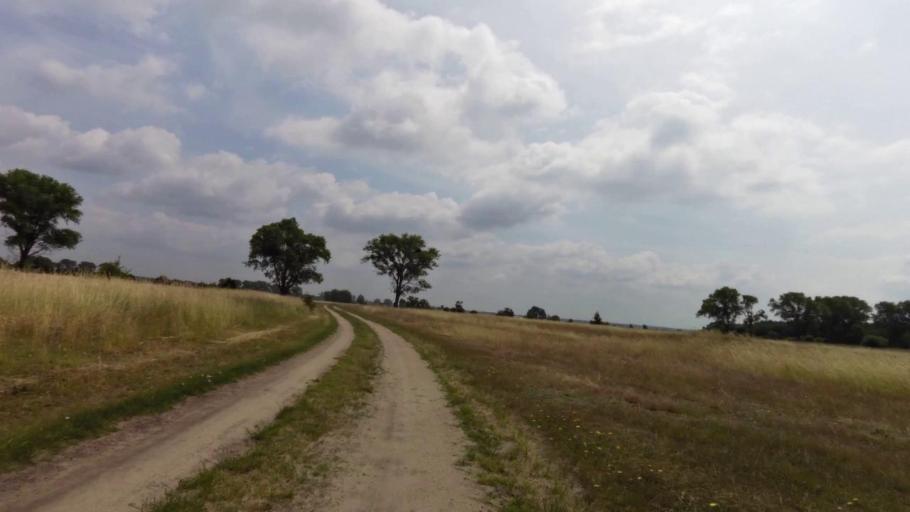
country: PL
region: West Pomeranian Voivodeship
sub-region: Powiat goleniowski
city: Goleniow
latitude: 53.4986
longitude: 14.7085
